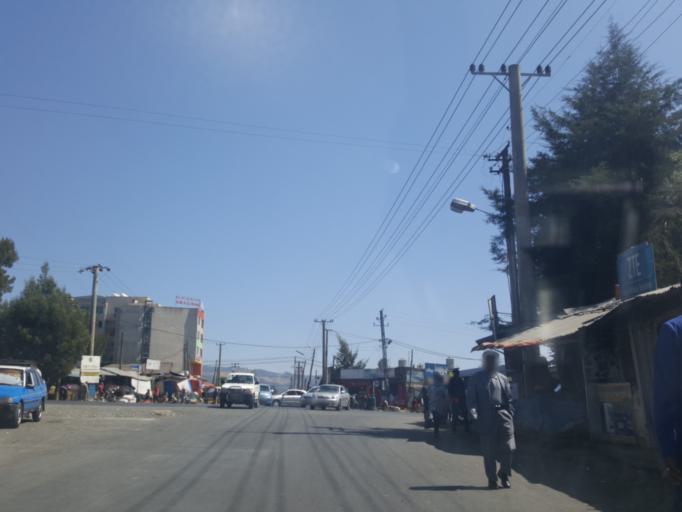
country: ET
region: Adis Abeba
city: Addis Ababa
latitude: 9.0530
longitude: 38.7420
